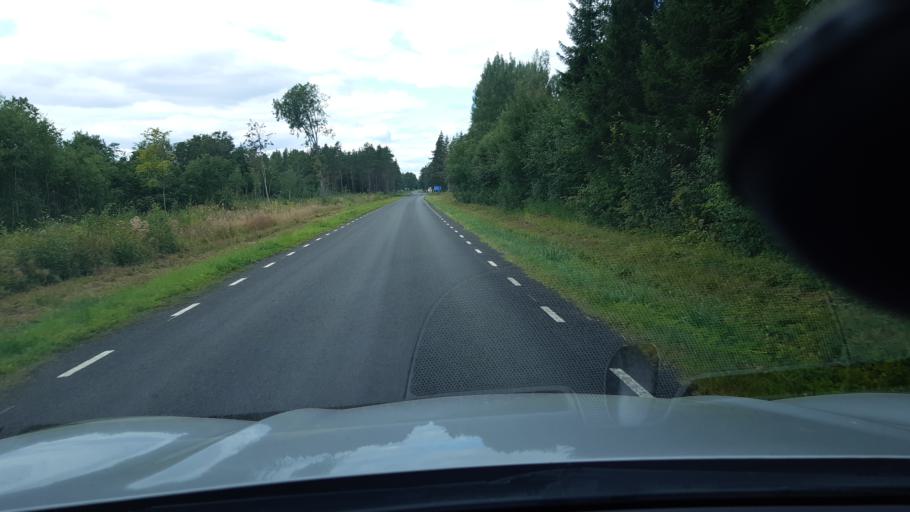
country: EE
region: Raplamaa
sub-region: Rapla vald
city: Rapla
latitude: 58.8847
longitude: 24.7294
